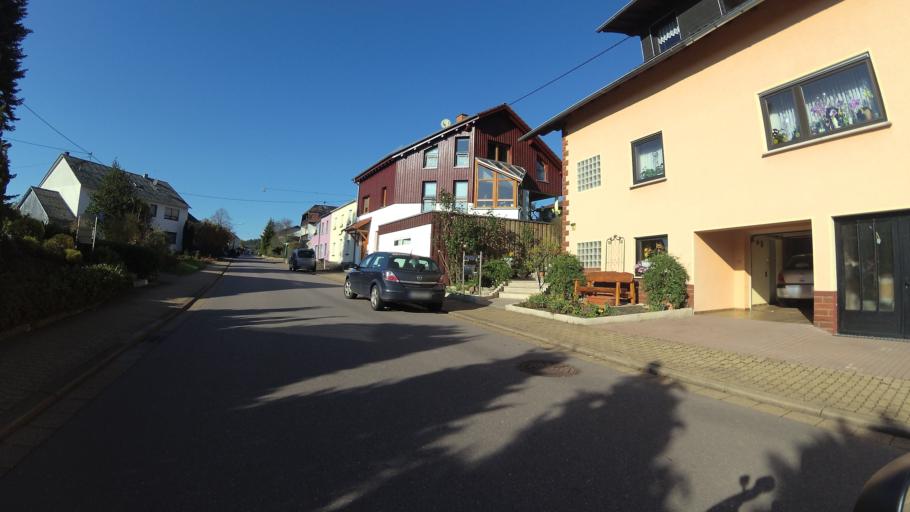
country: DE
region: Saarland
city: Britten
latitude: 49.4806
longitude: 6.7038
